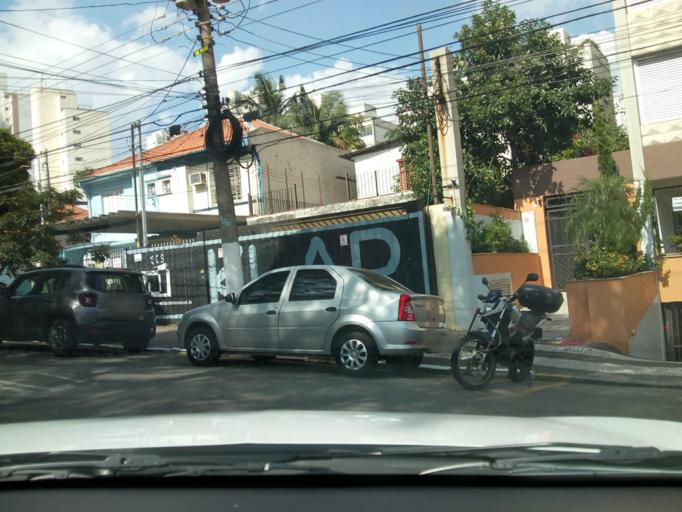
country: BR
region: Sao Paulo
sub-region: Sao Paulo
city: Sao Paulo
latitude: -23.5829
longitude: -46.6477
